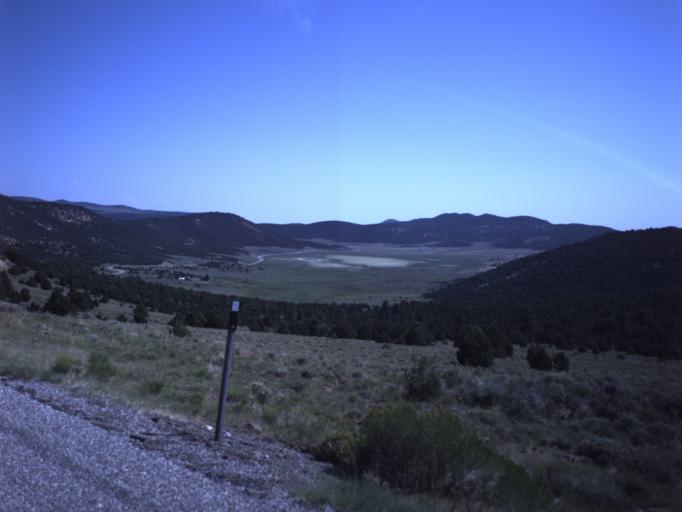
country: US
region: Utah
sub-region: Wayne County
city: Loa
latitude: 38.6046
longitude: -111.4621
